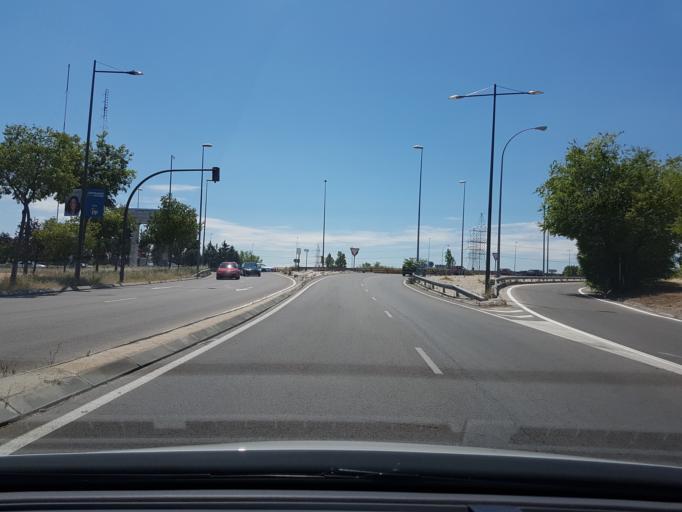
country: ES
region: Madrid
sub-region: Provincia de Madrid
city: Pozuelo de Alarcon
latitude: 40.4300
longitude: -3.8113
